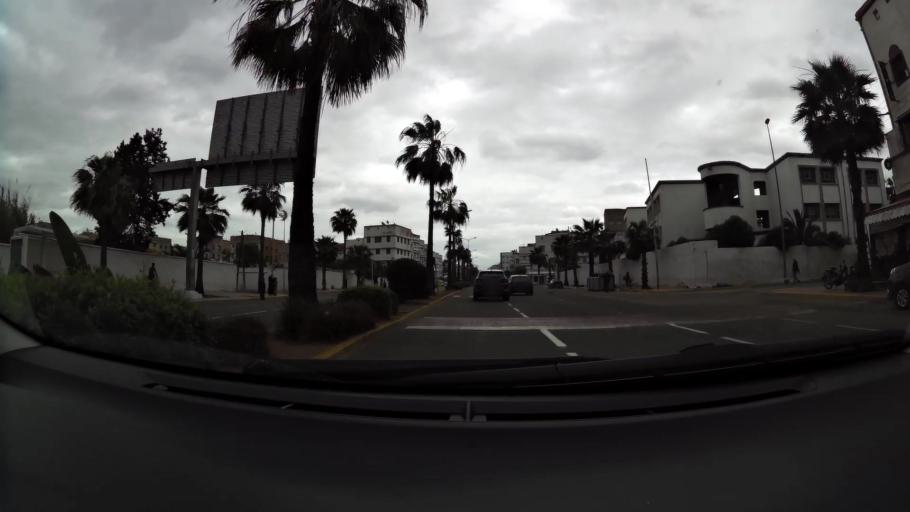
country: MA
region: Grand Casablanca
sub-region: Casablanca
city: Casablanca
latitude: 33.5659
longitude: -7.5718
